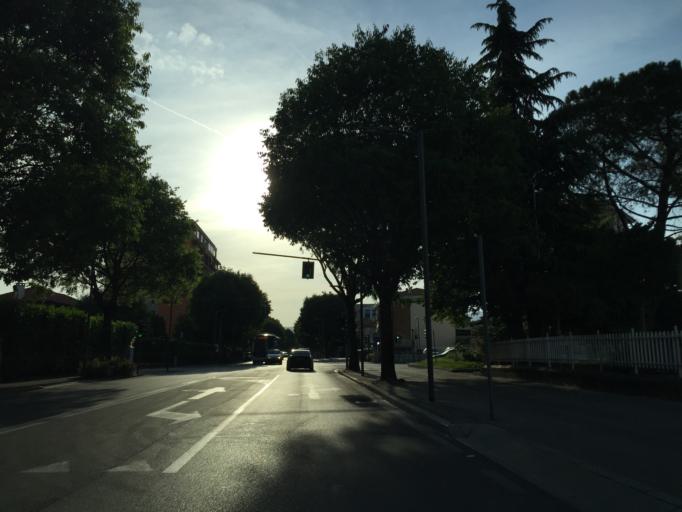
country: IT
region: Friuli Venezia Giulia
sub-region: Provincia di Pordenone
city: Pordenone
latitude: 45.9642
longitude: 12.6480
